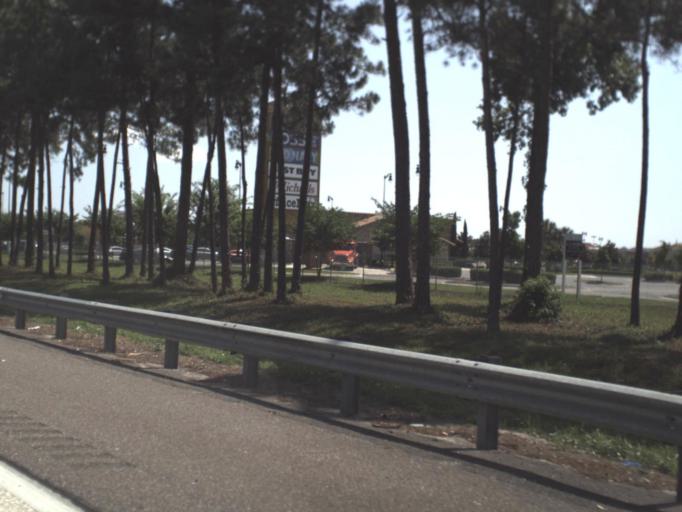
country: US
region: Florida
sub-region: Duval County
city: Jacksonville
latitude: 30.4732
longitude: -81.6454
